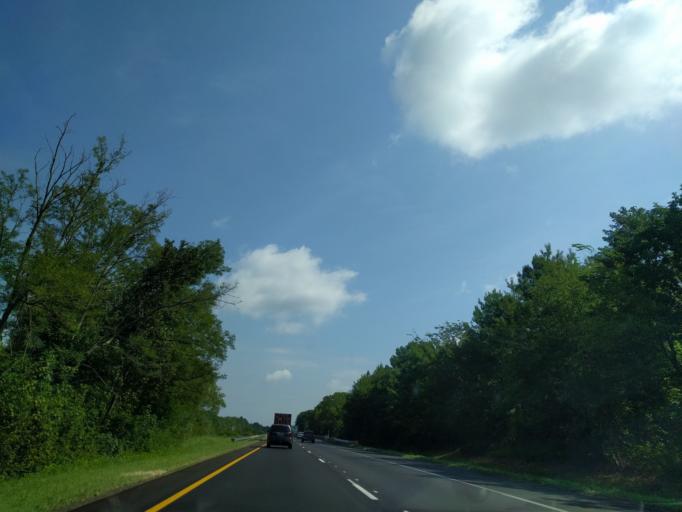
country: US
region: Tennessee
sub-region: Sumner County
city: White House
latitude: 36.4875
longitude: -86.6737
